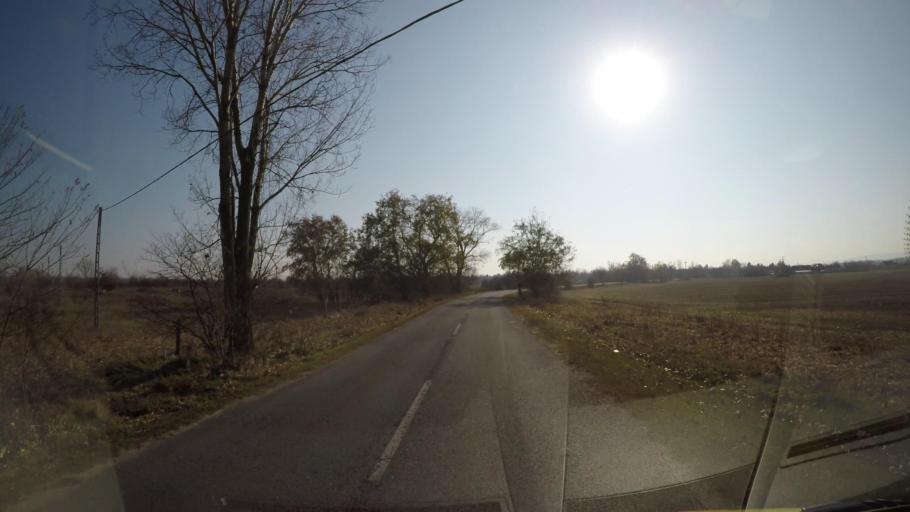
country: HU
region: Pest
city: Leanyfalu
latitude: 47.6962
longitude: 19.1040
